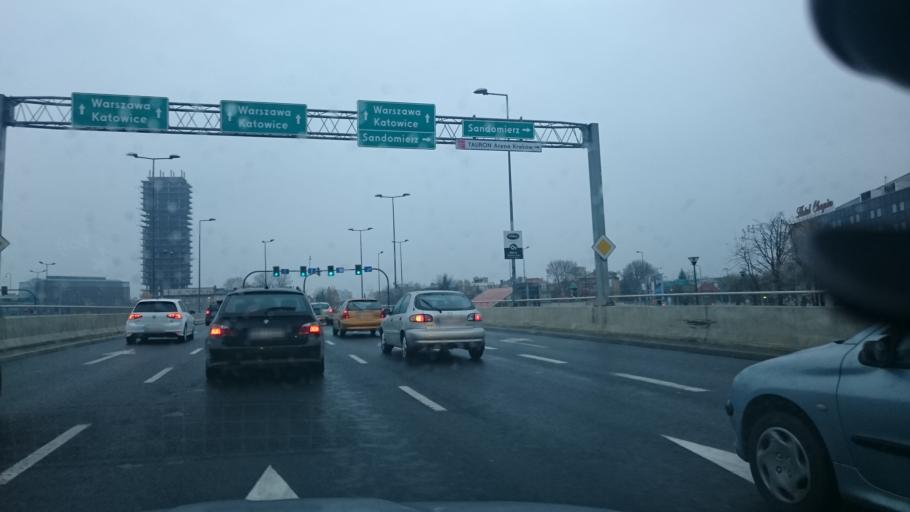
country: PL
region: Lesser Poland Voivodeship
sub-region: Krakow
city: Krakow
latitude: 50.0644
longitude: 19.9598
